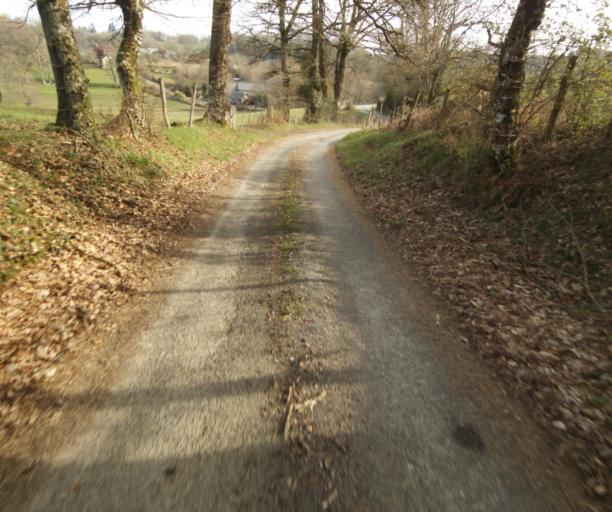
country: FR
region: Limousin
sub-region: Departement de la Correze
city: Chamboulive
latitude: 45.4428
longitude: 1.7532
